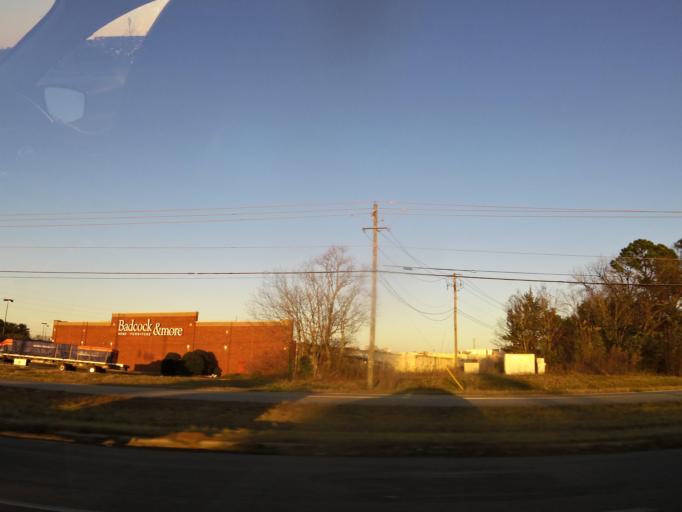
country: US
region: Alabama
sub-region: Montgomery County
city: Montgomery
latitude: 32.3248
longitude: -86.2394
